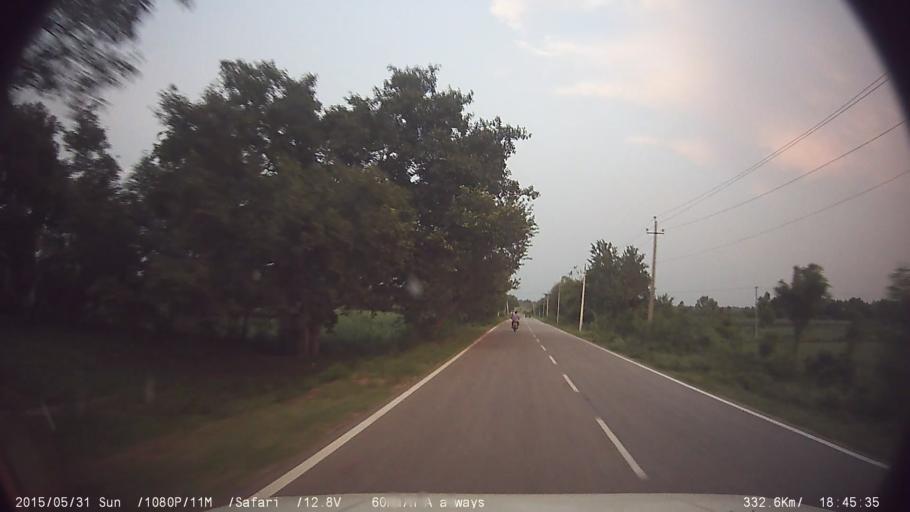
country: IN
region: Karnataka
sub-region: Mysore
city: Tirumakudal Narsipur
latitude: 12.1591
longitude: 76.8261
